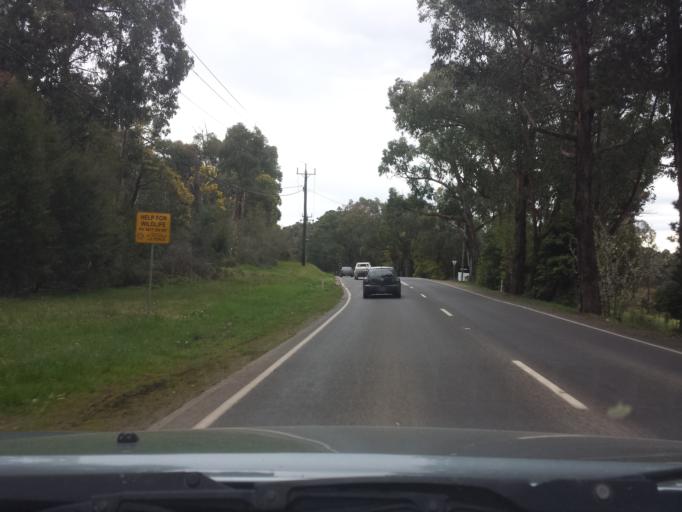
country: AU
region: Victoria
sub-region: Yarra Ranges
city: Mount Evelyn
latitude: -37.7991
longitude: 145.3950
